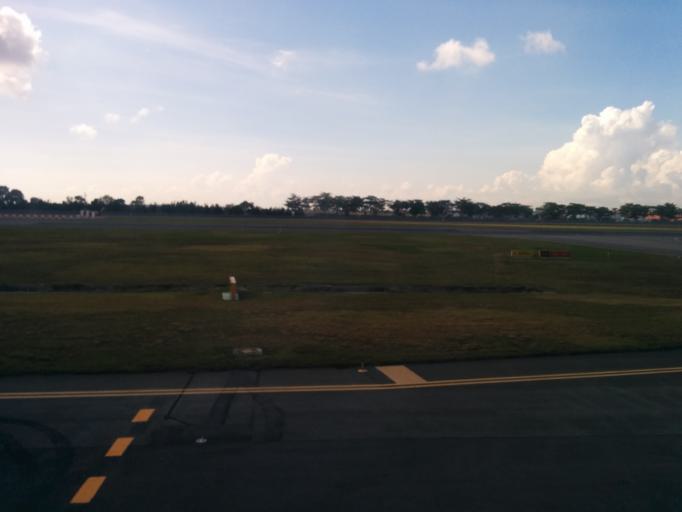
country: SG
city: Singapore
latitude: 1.3315
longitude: 103.9841
